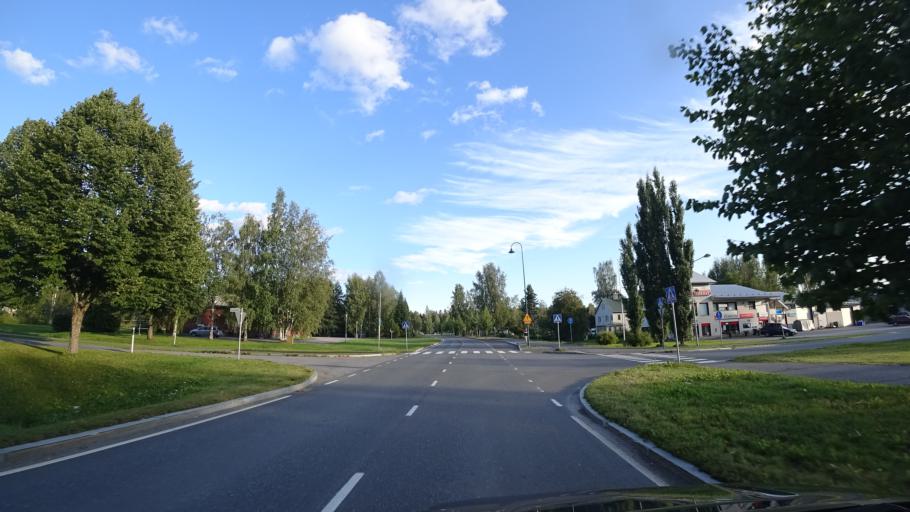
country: FI
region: Haeme
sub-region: Haemeenlinna
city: Lammi
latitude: 61.0751
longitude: 25.0113
